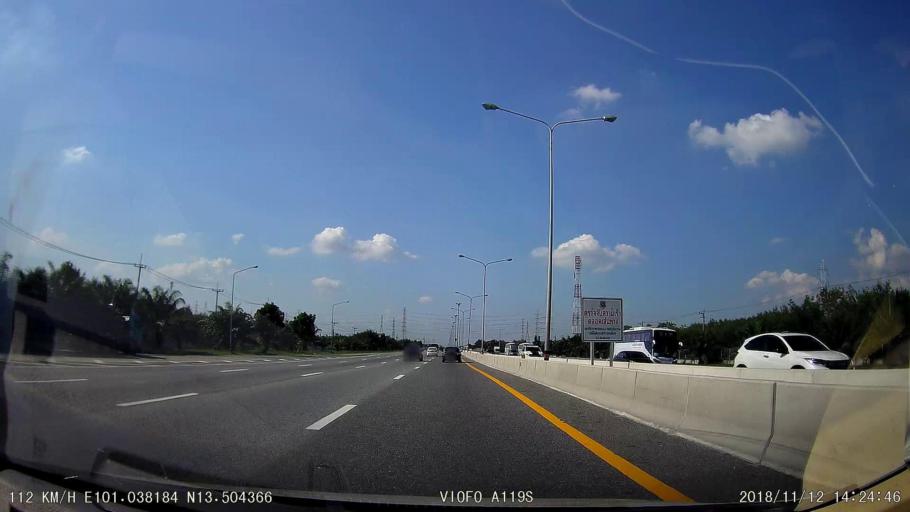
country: TH
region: Chachoengsao
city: Bang Pakong
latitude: 13.5045
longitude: 101.0381
